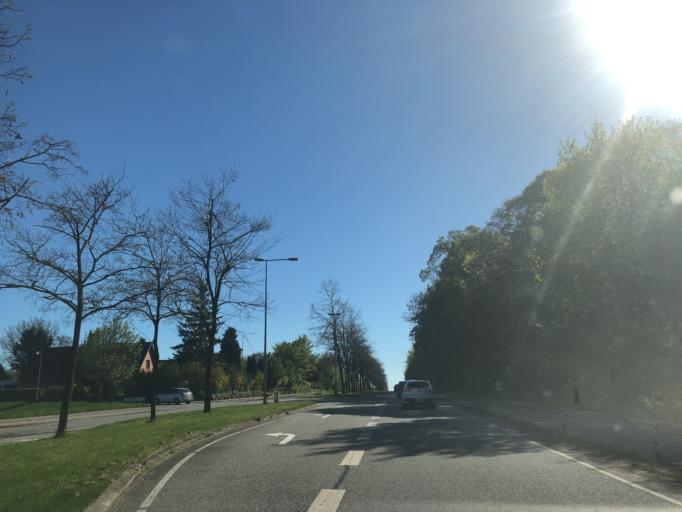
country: DK
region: Zealand
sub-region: Koge Kommune
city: Koge
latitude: 55.4213
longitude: 12.1454
